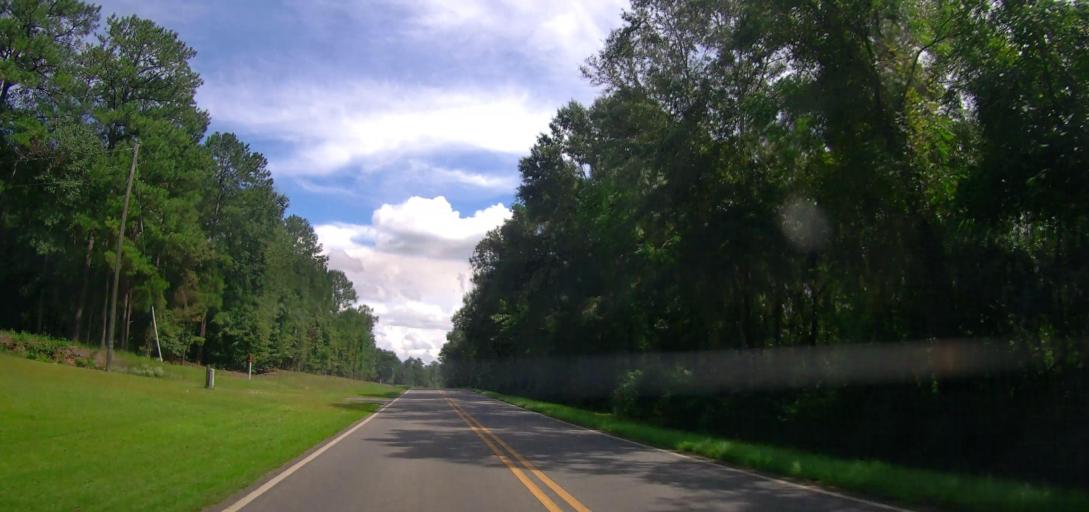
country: US
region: Georgia
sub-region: Taylor County
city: Butler
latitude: 32.5349
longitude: -84.2152
